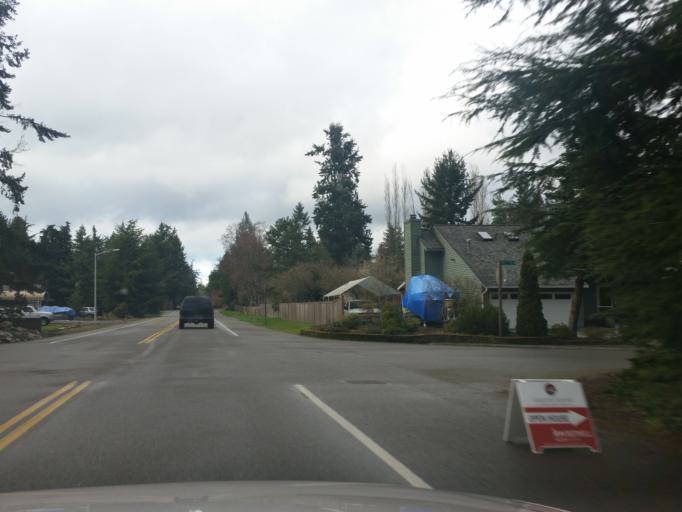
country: US
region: Washington
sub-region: Snohomish County
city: Meadowdale
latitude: 47.8614
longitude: -122.3091
